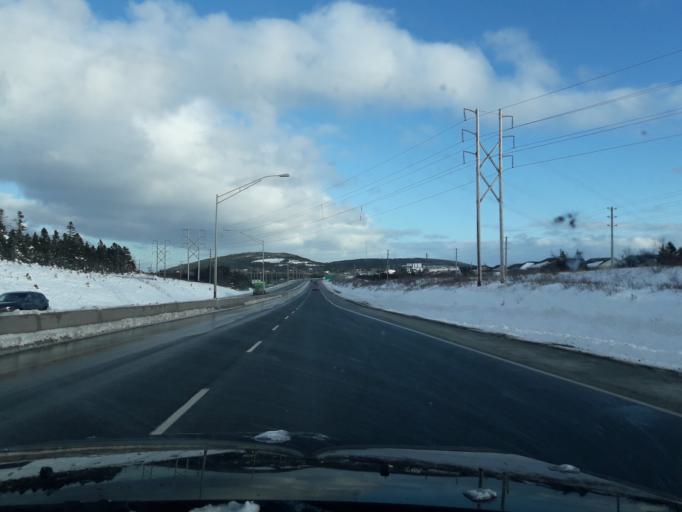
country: CA
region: Newfoundland and Labrador
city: St. John's
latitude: 47.6132
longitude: -52.7059
